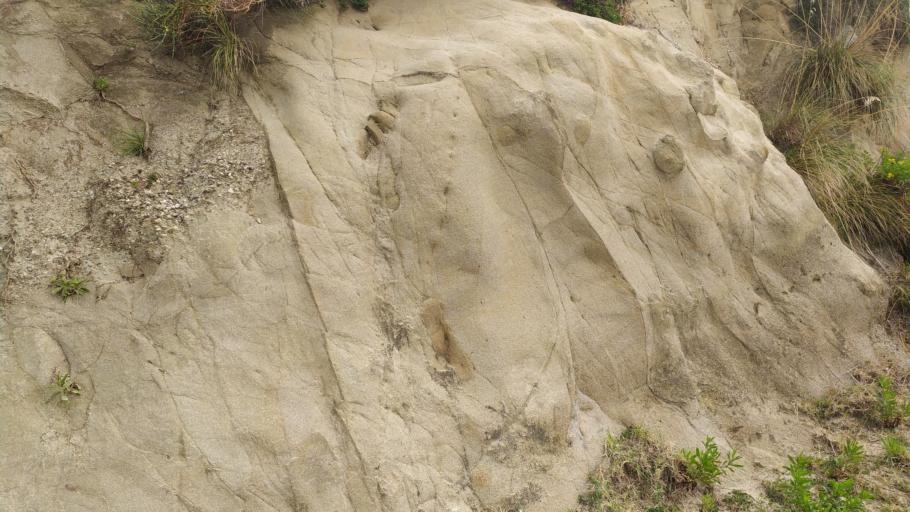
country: IT
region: Sicily
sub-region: Messina
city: Saponara
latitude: 38.2117
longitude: 15.4779
